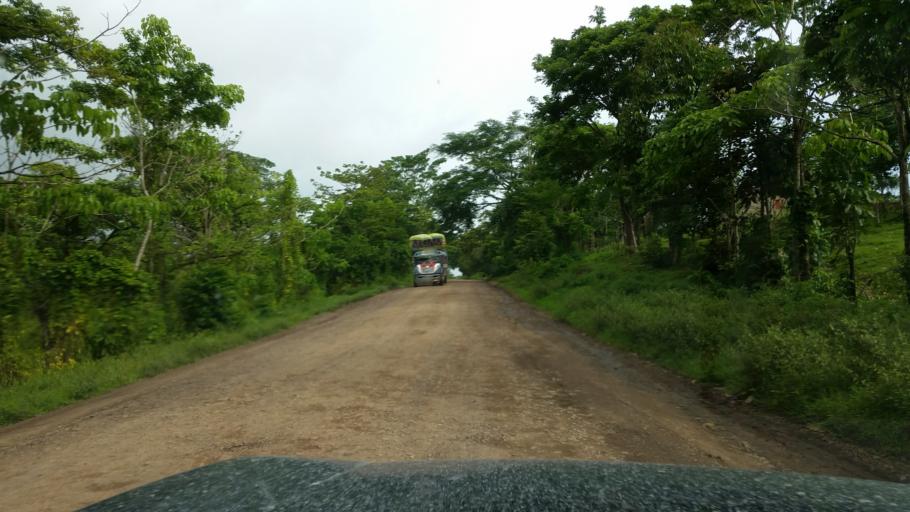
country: NI
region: Atlantico Norte (RAAN)
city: Siuna
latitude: 13.4237
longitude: -84.8530
